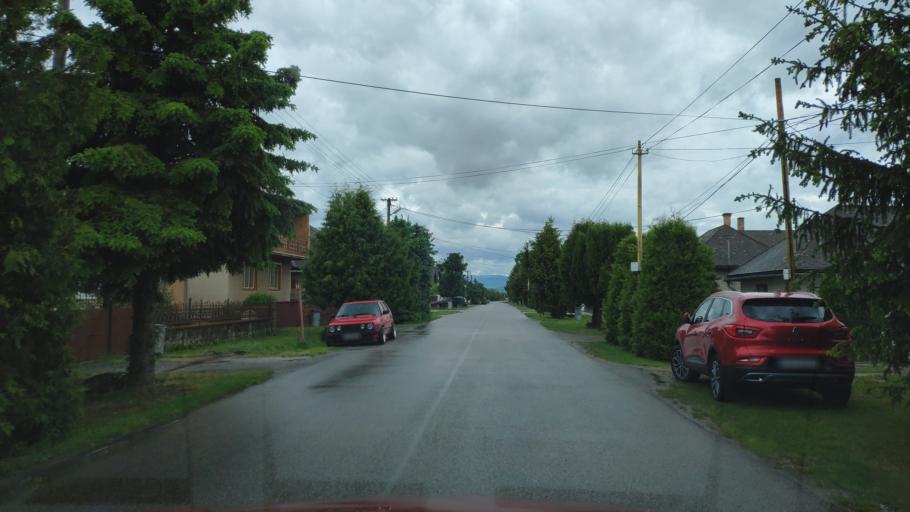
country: SK
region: Kosicky
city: Moldava nad Bodvou
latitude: 48.5349
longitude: 21.1096
